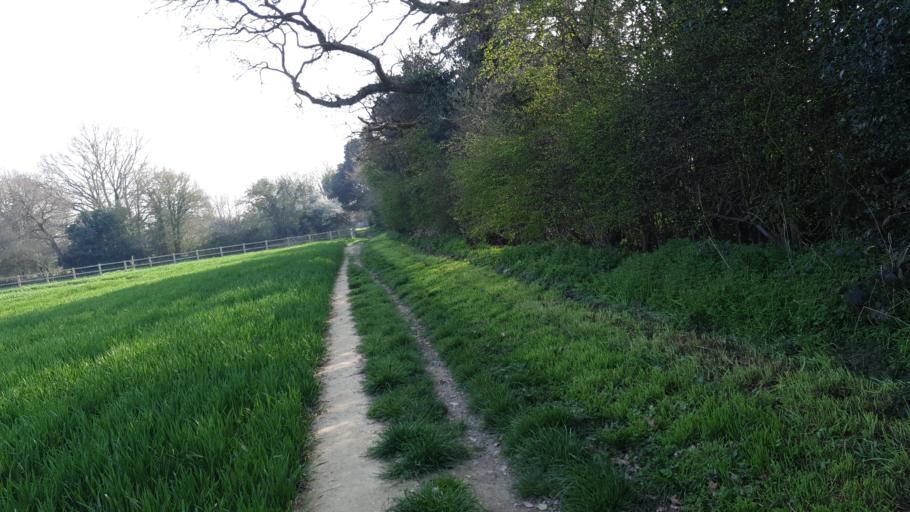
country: GB
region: England
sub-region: Essex
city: Little Clacton
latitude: 51.8770
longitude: 1.1179
